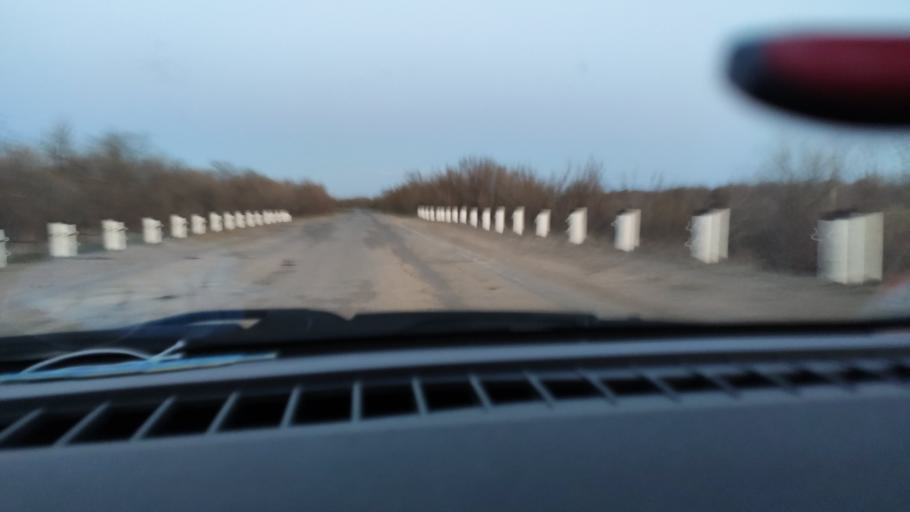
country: RU
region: Saratov
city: Krasnoarmeysk
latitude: 51.0708
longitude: 45.9888
